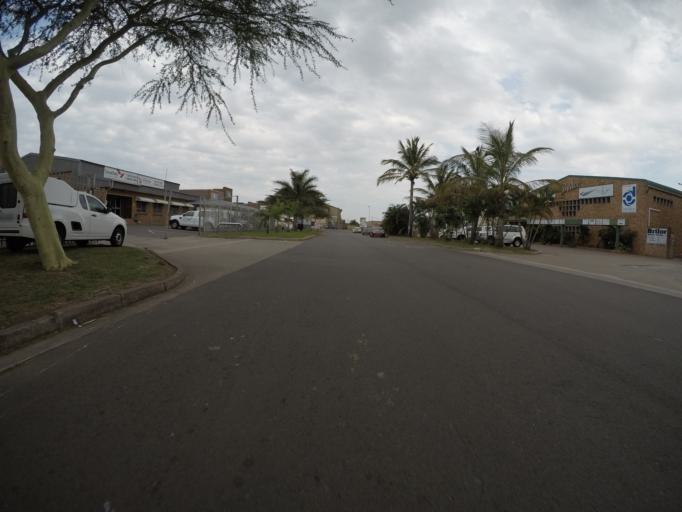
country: ZA
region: KwaZulu-Natal
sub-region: uThungulu District Municipality
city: Richards Bay
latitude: -28.7592
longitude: 32.0418
